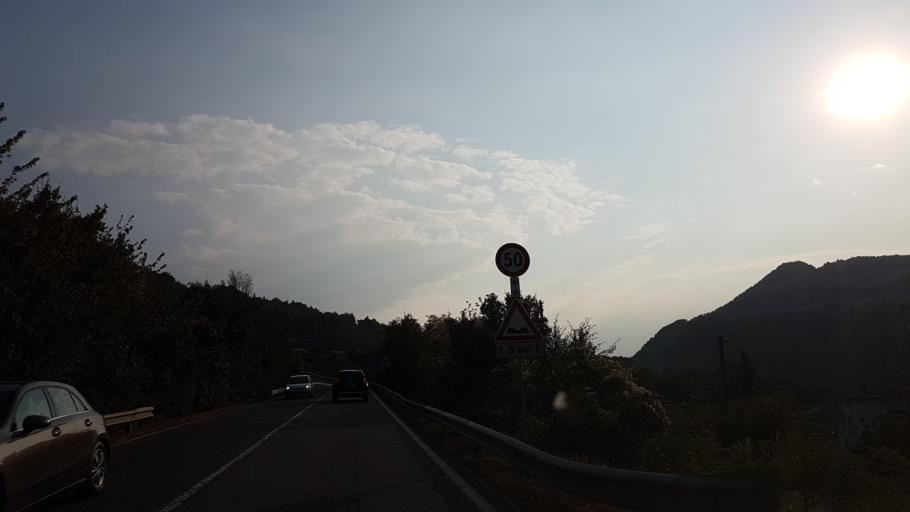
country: IT
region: Emilia-Romagna
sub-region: Provincia di Parma
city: Solignano
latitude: 44.6248
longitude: 10.0080
